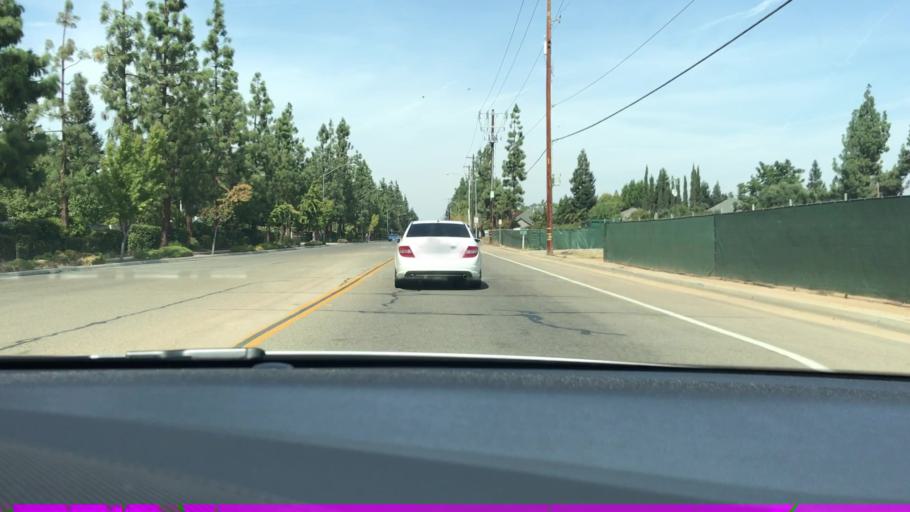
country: US
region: California
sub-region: Fresno County
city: Clovis
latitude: 36.8527
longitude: -119.7657
